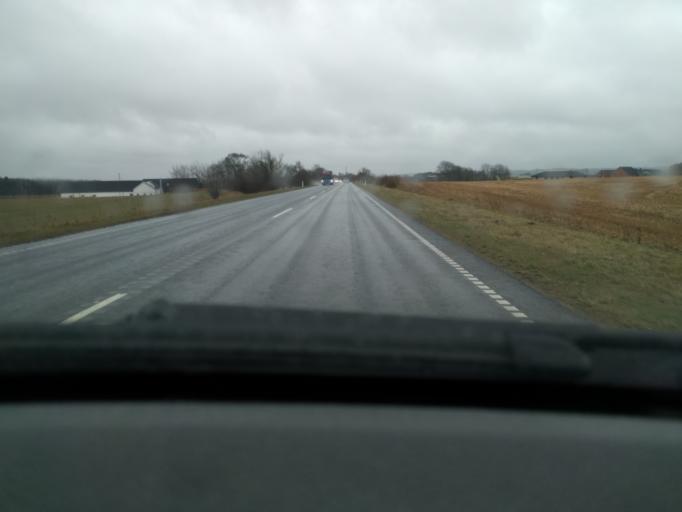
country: DK
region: Central Jutland
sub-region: Silkeborg Kommune
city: Kjellerup
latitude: 56.2626
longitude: 9.4329
